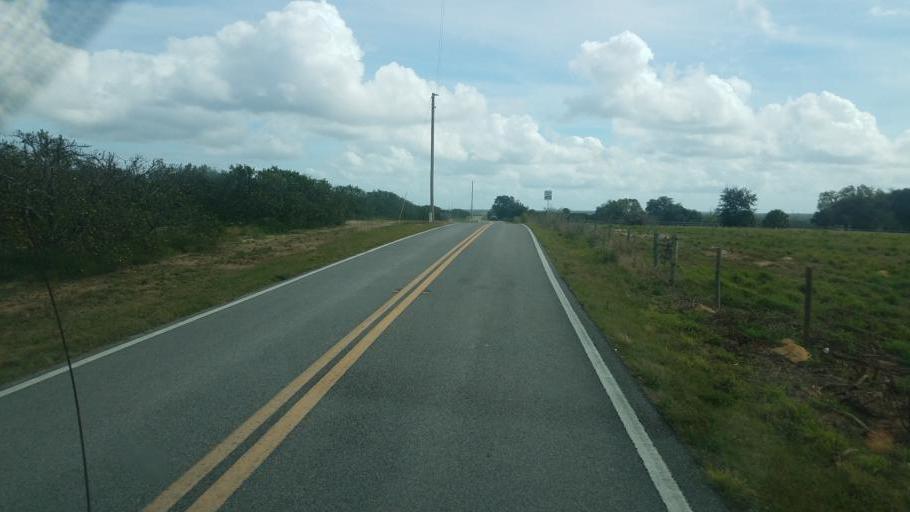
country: US
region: Florida
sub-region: Polk County
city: Dundee
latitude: 28.0334
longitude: -81.5949
